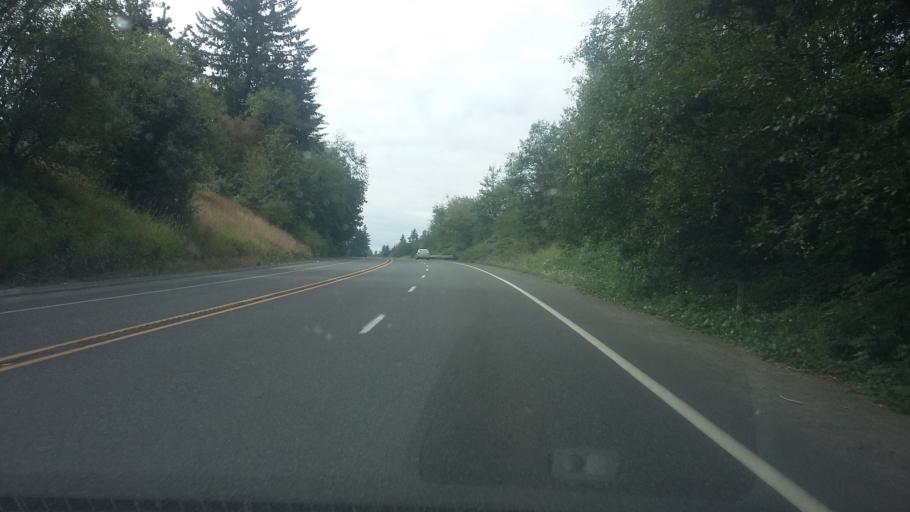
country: US
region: Washington
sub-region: Clark County
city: Lewisville
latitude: 45.8047
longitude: -122.5493
